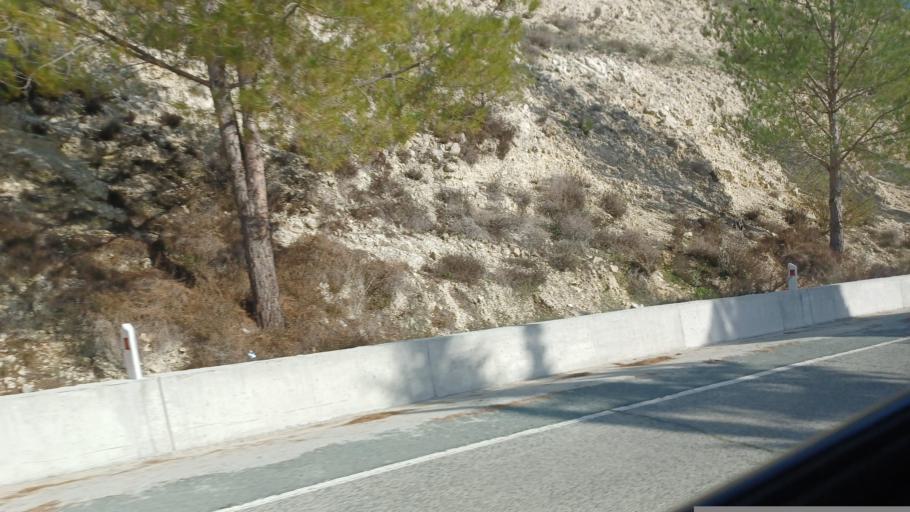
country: CY
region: Limassol
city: Pachna
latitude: 34.8362
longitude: 32.7944
